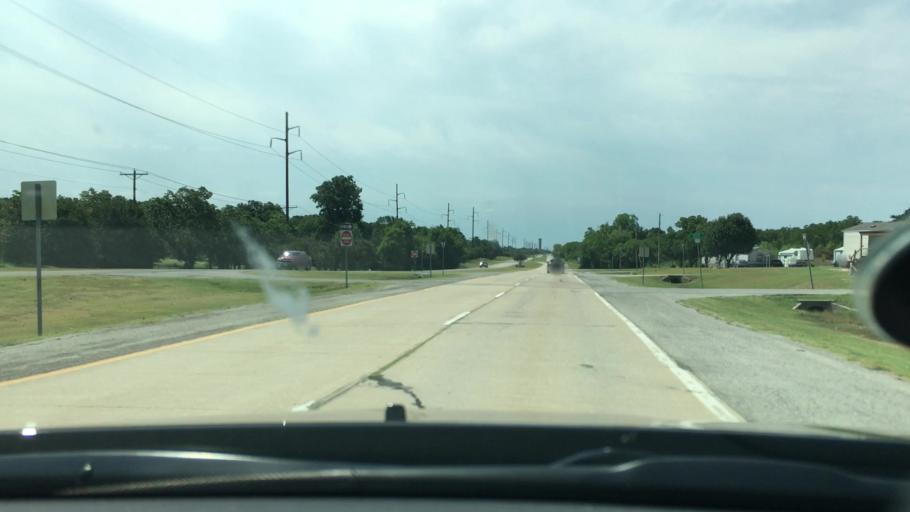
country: US
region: Oklahoma
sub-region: Carter County
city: Ardmore
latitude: 34.2207
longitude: -97.1433
